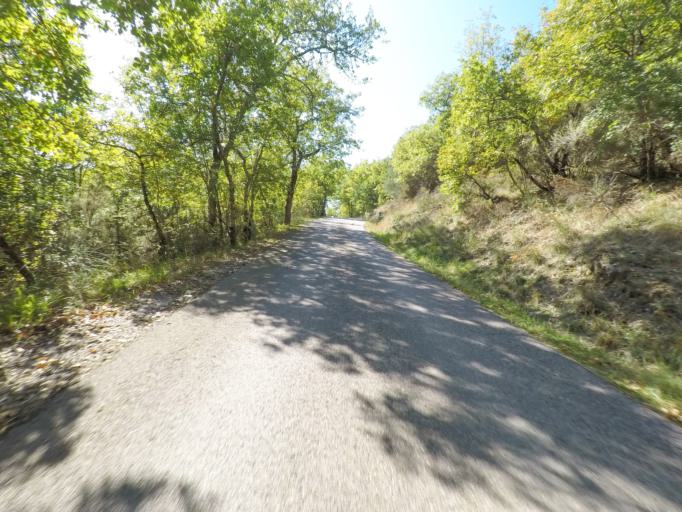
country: IT
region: Tuscany
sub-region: Provincia di Siena
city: Castellina in Chianti
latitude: 43.4302
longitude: 11.3369
